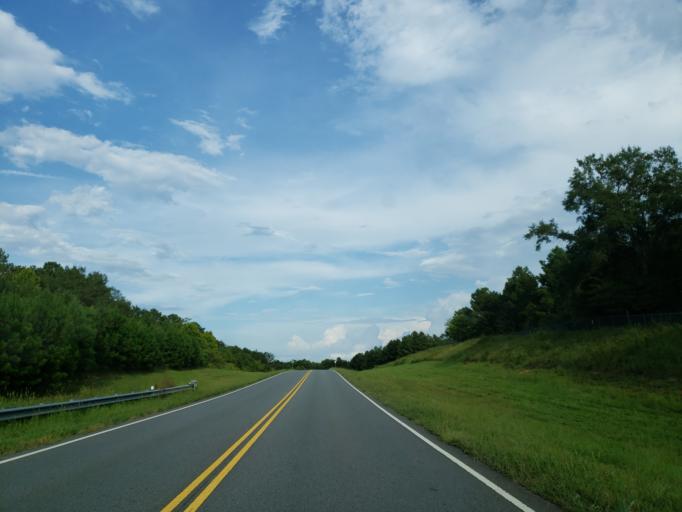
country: US
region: Georgia
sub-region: Bartow County
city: Euharlee
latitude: 34.1368
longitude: -84.9317
